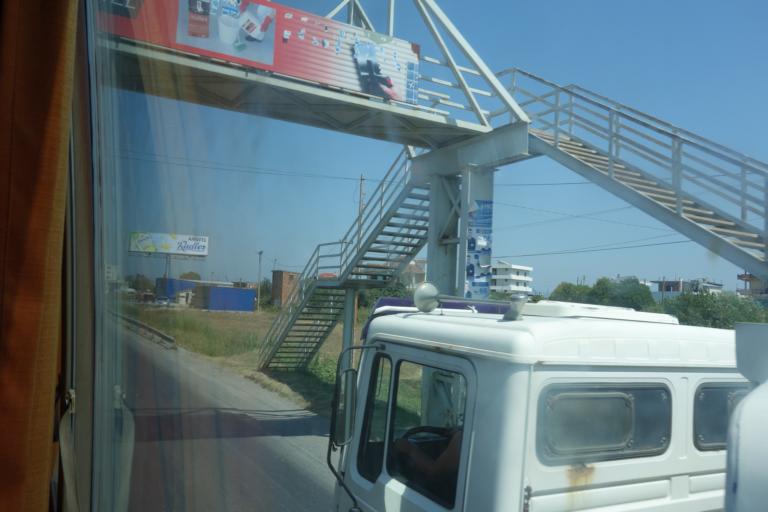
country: AL
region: Durres
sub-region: Rrethi i Durresit
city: Rrashbull
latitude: 41.3410
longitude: 19.4927
